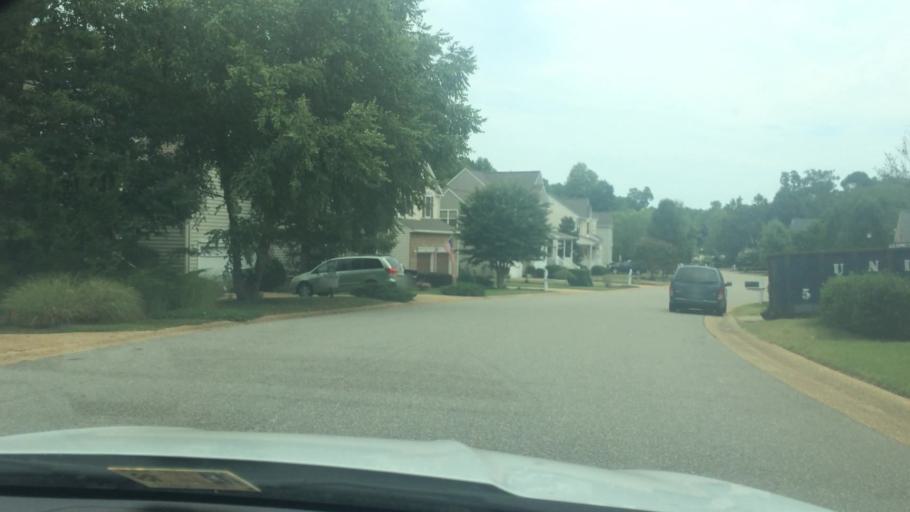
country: US
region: Virginia
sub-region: James City County
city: Williamsburg
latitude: 37.2731
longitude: -76.8170
